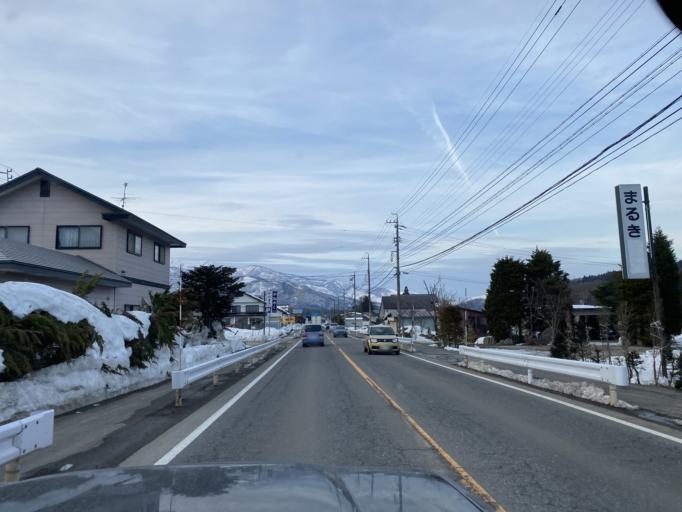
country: JP
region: Nagano
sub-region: Kitaazumi Gun
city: Hakuba
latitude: 36.6629
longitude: 137.8489
